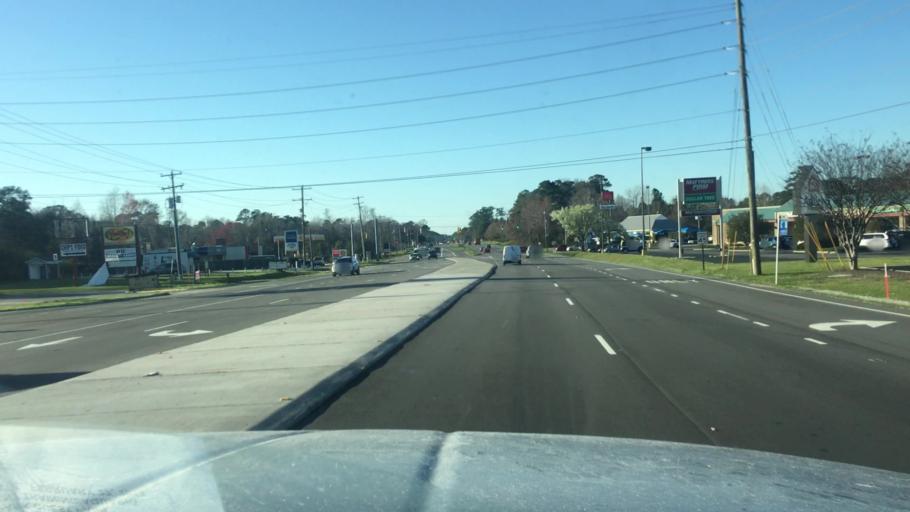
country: US
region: North Carolina
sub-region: New Hanover County
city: Myrtle Grove
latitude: 34.1414
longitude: -77.8949
